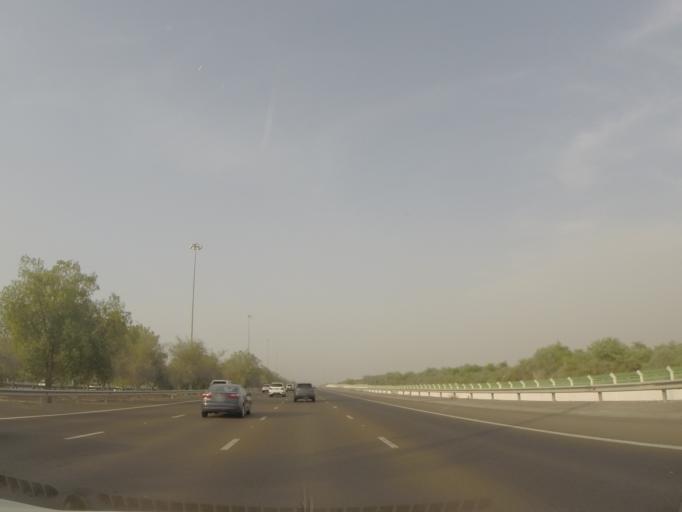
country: AE
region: Abu Dhabi
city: Abu Dhabi
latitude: 24.7159
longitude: 54.8016
